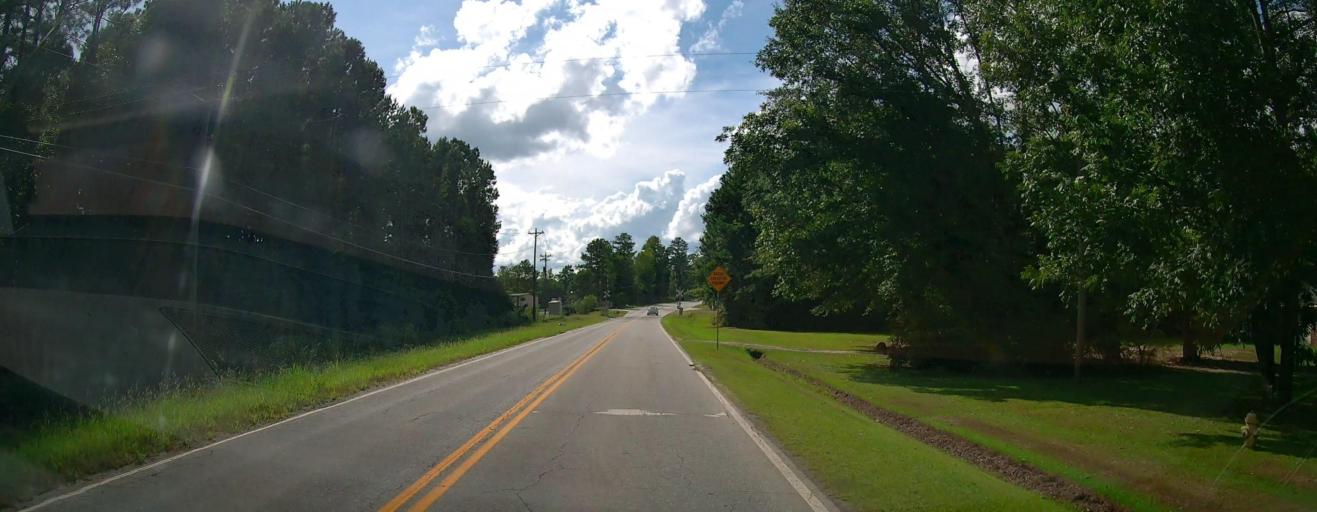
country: US
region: Alabama
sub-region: Russell County
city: Phenix City
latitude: 32.5930
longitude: -84.9431
